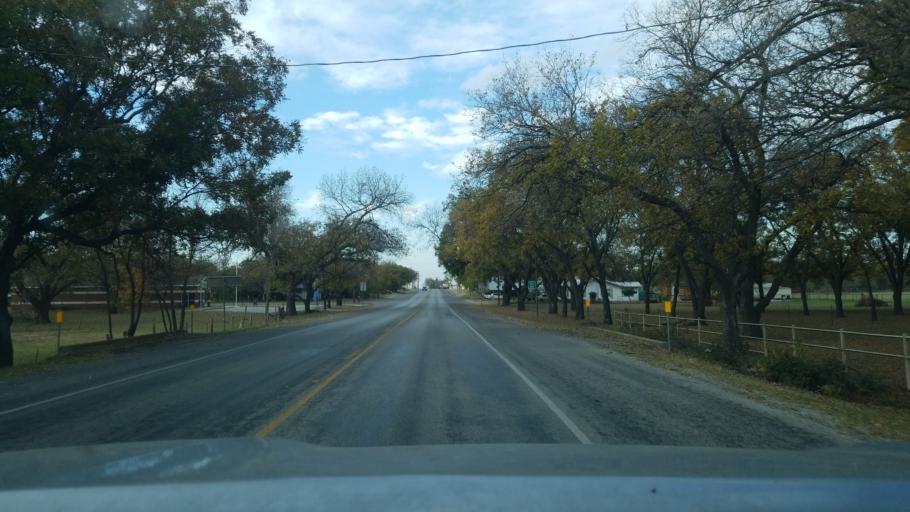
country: US
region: Texas
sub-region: Brown County
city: Lake Brownwood
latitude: 31.9756
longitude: -98.9204
